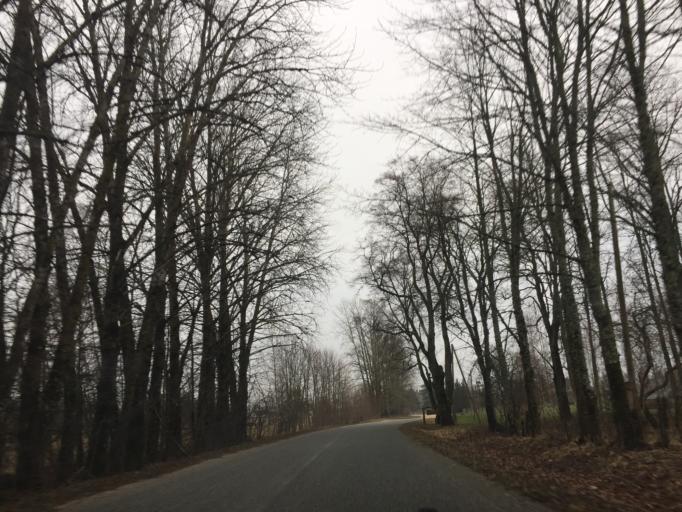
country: LV
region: Limbazu Rajons
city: Limbazi
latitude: 57.6044
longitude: 24.6112
